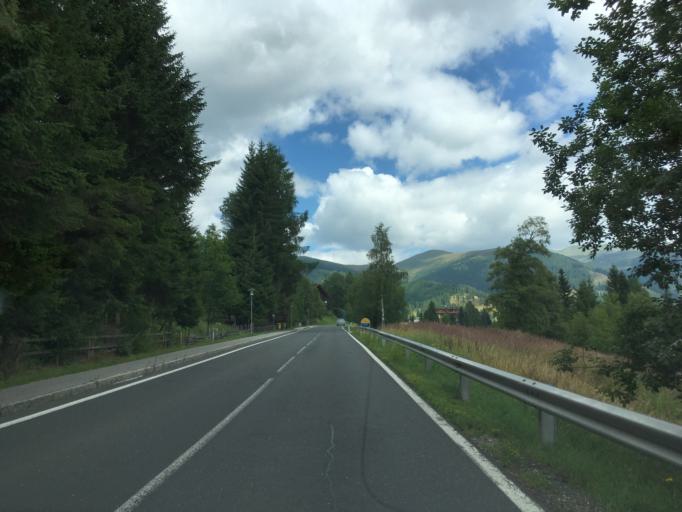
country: AT
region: Carinthia
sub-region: Politischer Bezirk Spittal an der Drau
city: Kleinkirchheim
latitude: 46.8315
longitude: 13.7637
